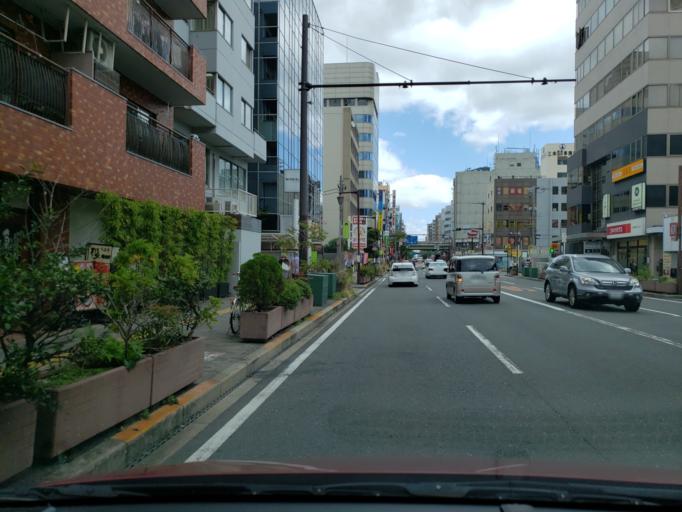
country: JP
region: Osaka
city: Suita
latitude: 34.7576
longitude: 135.4942
